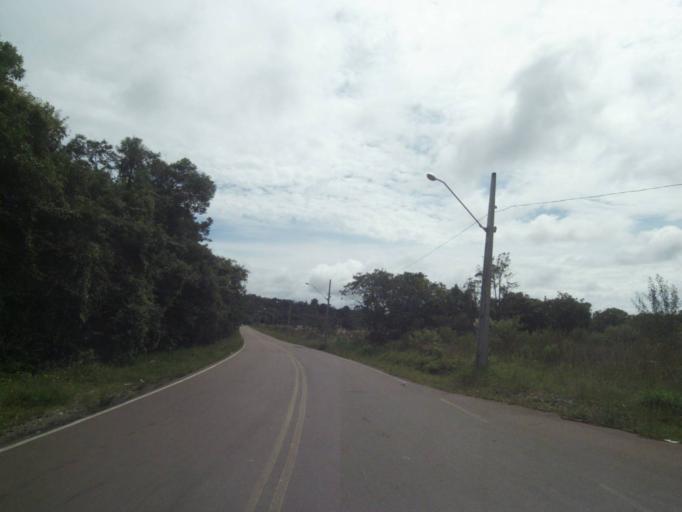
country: BR
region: Parana
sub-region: Campina Grande Do Sul
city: Campina Grande do Sul
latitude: -25.3144
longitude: -49.0204
